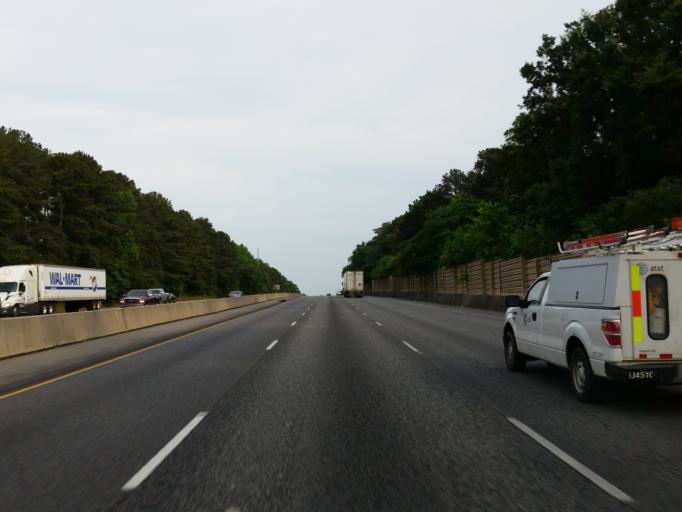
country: US
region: Georgia
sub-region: Bibb County
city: West Point
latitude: 32.8752
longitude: -83.7639
